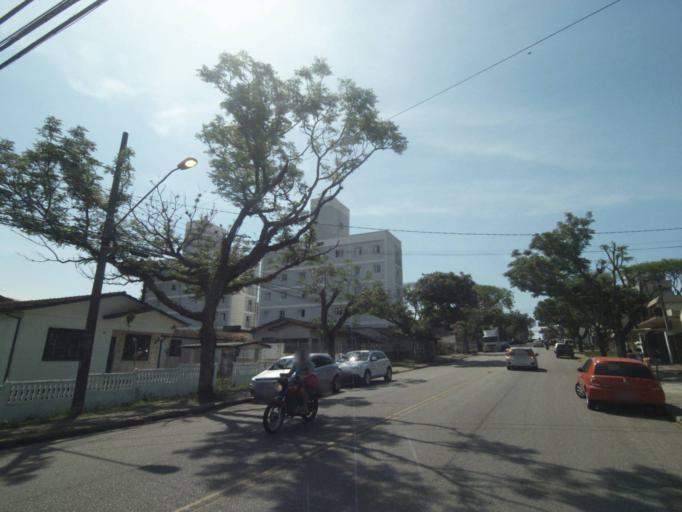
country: BR
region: Parana
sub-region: Curitiba
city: Curitiba
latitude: -25.4768
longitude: -49.2969
